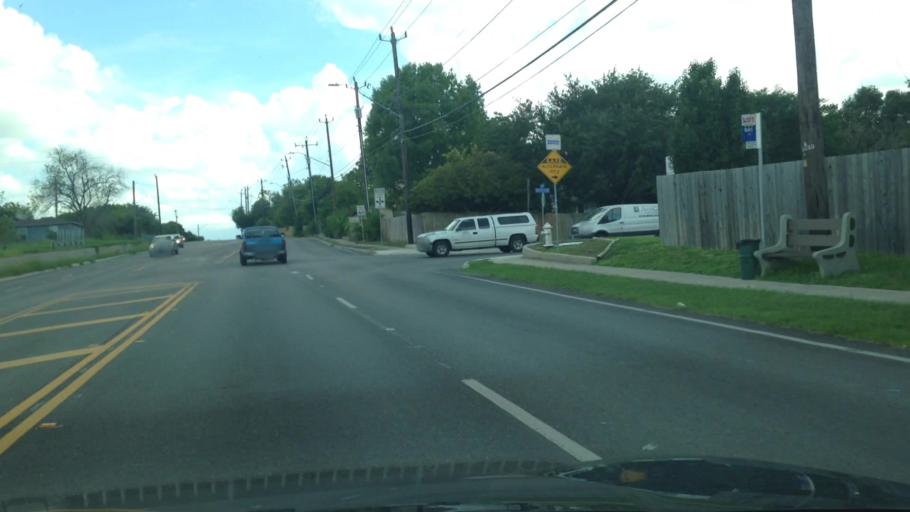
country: US
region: Texas
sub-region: Bexar County
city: Windcrest
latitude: 29.5730
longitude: -98.3977
